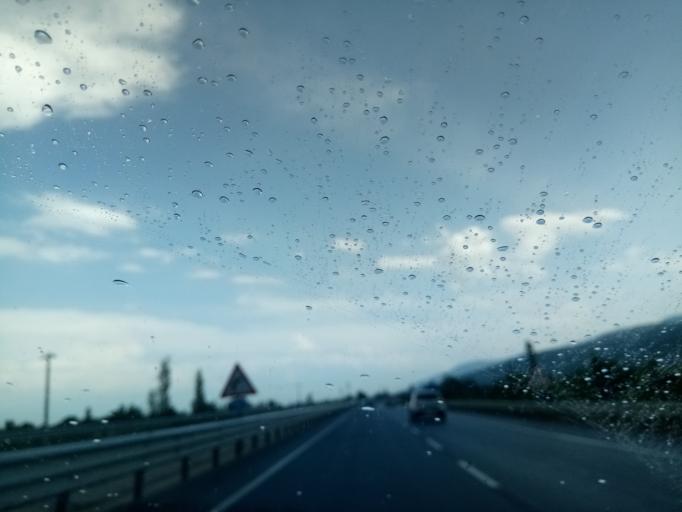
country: TR
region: Afyonkarahisar
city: Sultandagi
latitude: 38.4627
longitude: 31.3047
